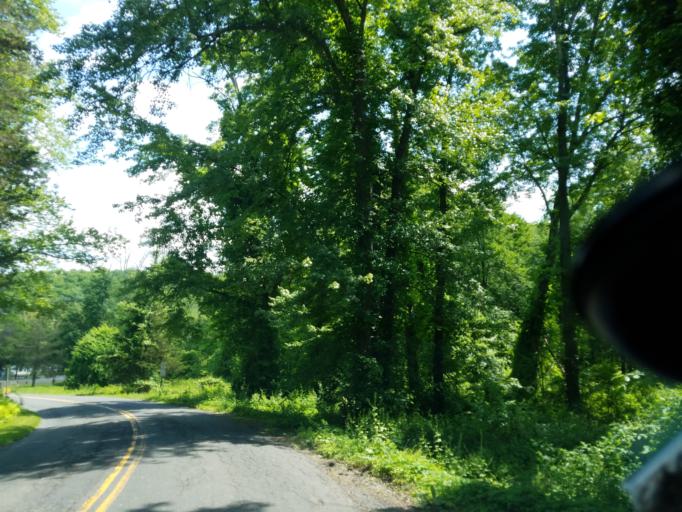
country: US
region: Connecticut
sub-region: Fairfield County
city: Sherman
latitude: 41.5083
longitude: -73.4736
